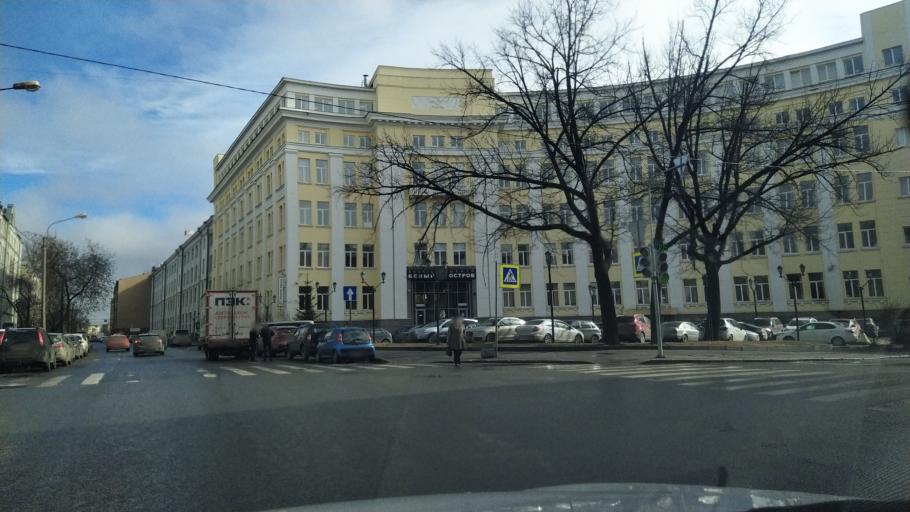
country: RU
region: Leningrad
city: Chernaya Rechka
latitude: 59.9879
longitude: 30.3139
